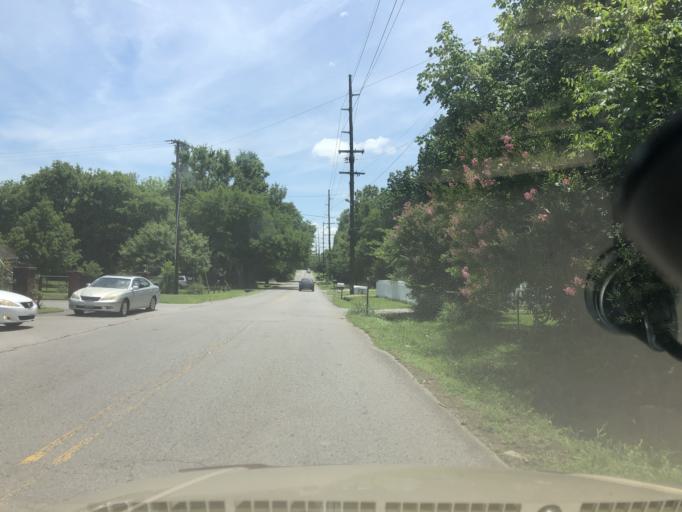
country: US
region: Tennessee
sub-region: Davidson County
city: Goodlettsville
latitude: 36.2594
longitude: -86.7038
